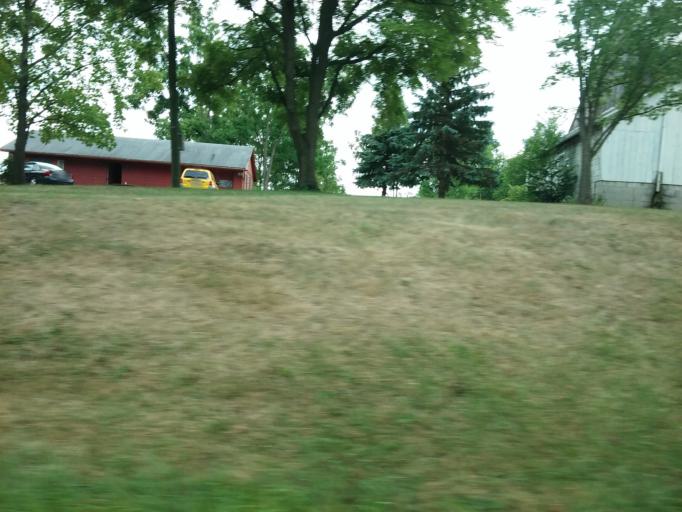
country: US
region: Ohio
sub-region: Hancock County
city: Findlay
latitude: 41.0536
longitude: -83.6762
